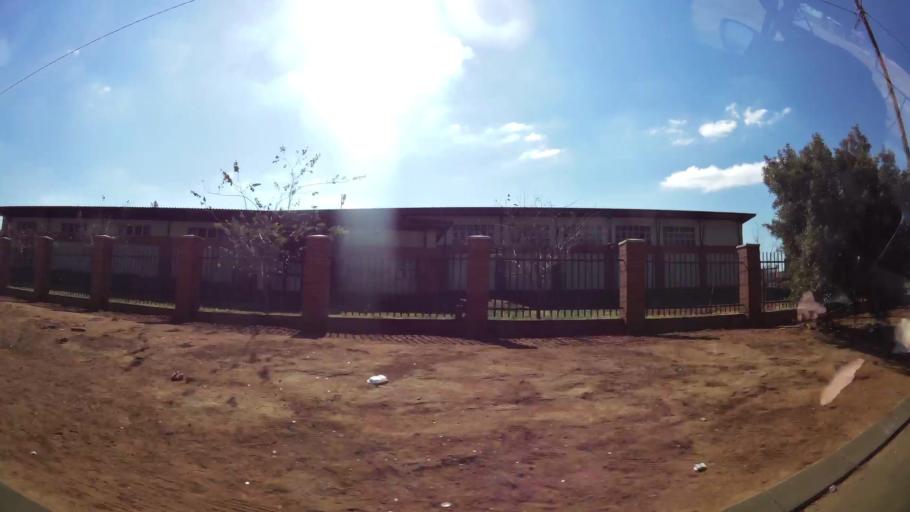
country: ZA
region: Gauteng
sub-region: West Rand District Municipality
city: Randfontein
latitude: -26.1686
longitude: 27.7779
